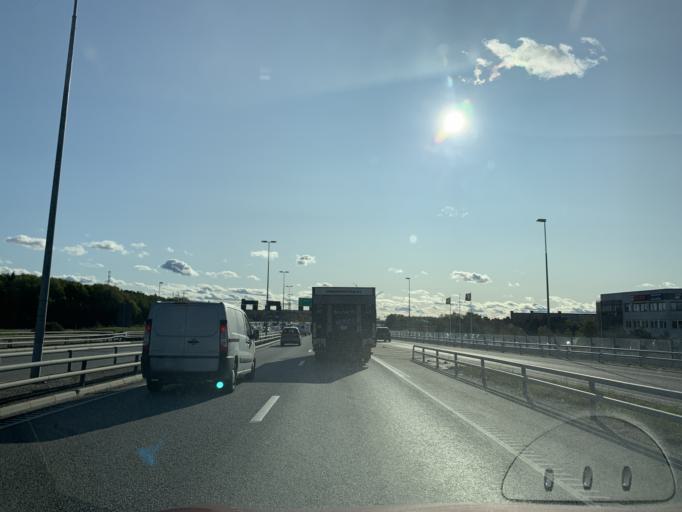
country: SE
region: Stockholm
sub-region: Stockholms Kommun
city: Kista
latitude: 59.3955
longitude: 17.9505
